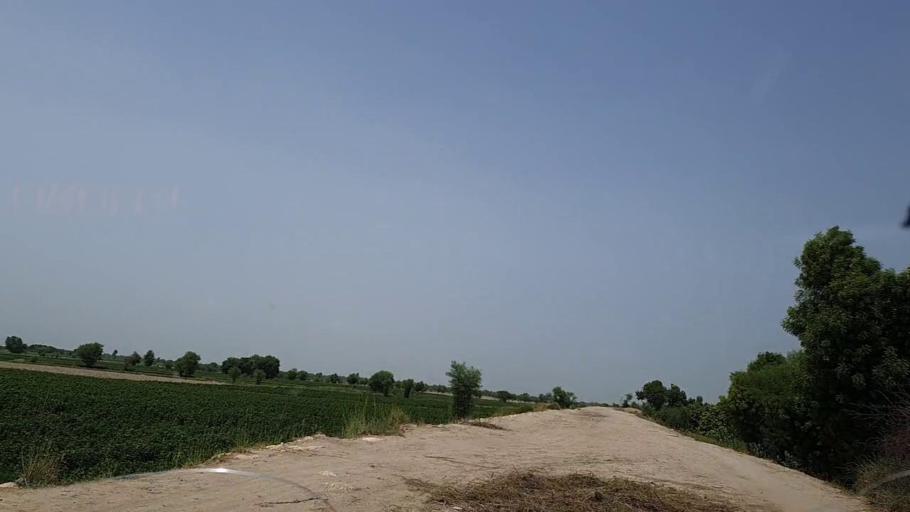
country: PK
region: Sindh
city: Tharu Shah
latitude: 27.0117
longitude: 68.1018
